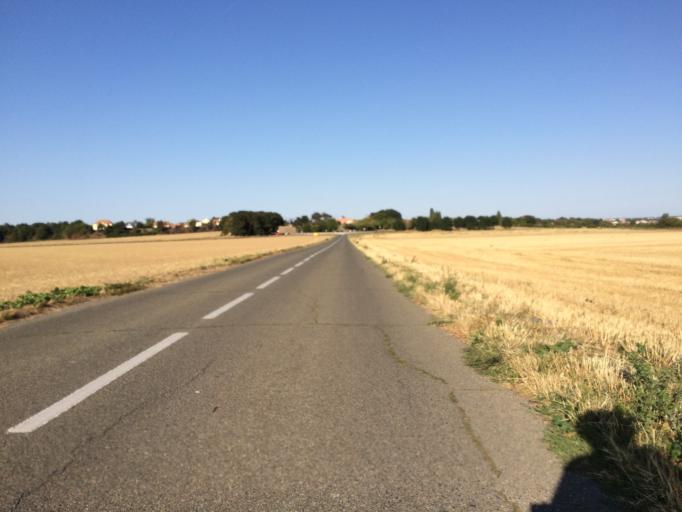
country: FR
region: Ile-de-France
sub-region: Departement de l'Essonne
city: Epinay-sur-Orge
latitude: 48.6684
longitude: 2.3051
